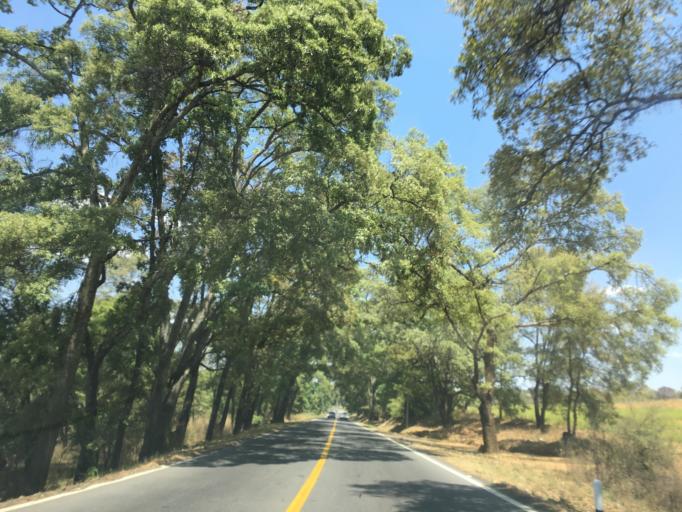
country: MX
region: Michoacan
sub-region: Chilchota
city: Tacuro (Santa Maria Tacuro)
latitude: 19.7986
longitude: -102.0250
